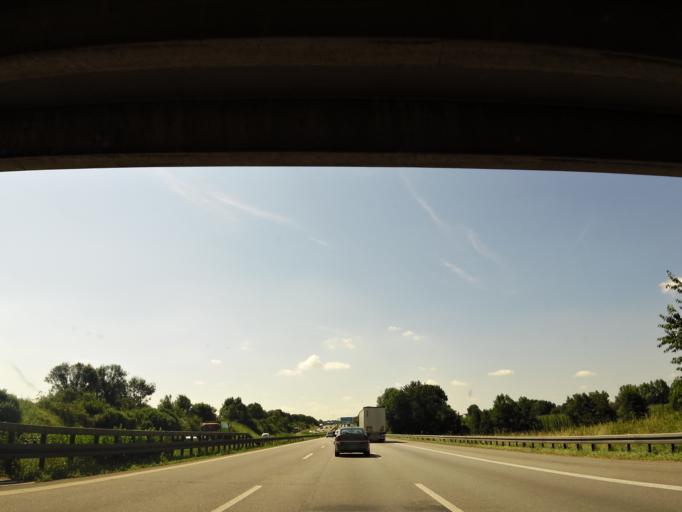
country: DE
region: Bavaria
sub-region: Upper Bavaria
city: Reichertshofen
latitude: 48.6590
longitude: 11.5120
